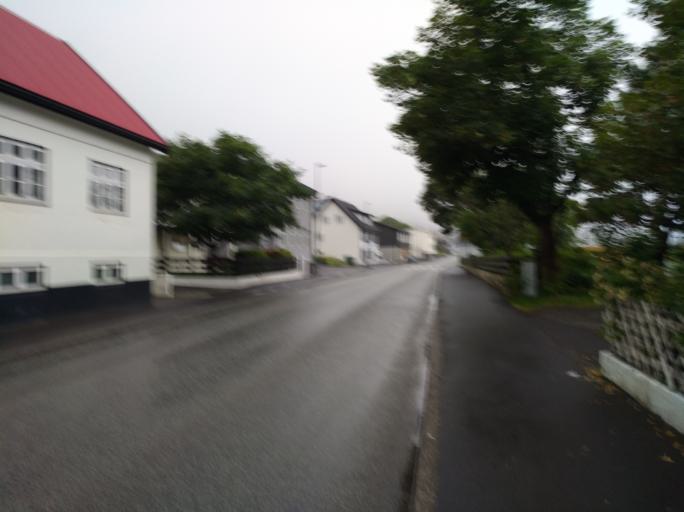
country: FO
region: Nordoyar
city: Klaksvik
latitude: 62.2281
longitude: -6.5921
